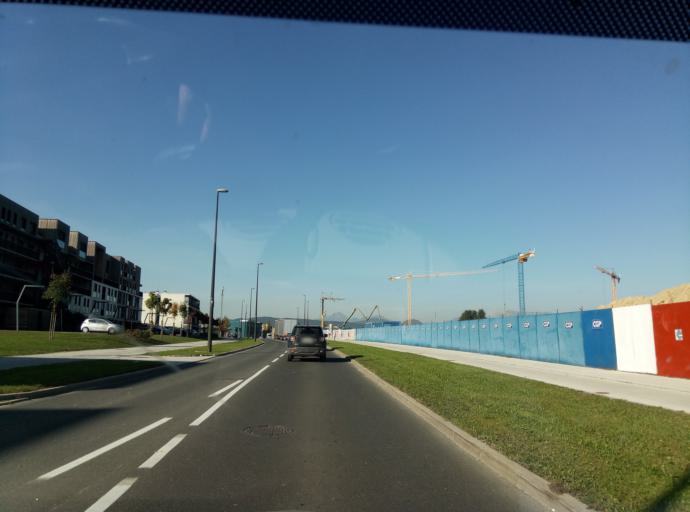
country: SI
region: Ljubljana
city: Ljubljana
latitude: 46.0436
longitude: 14.4626
